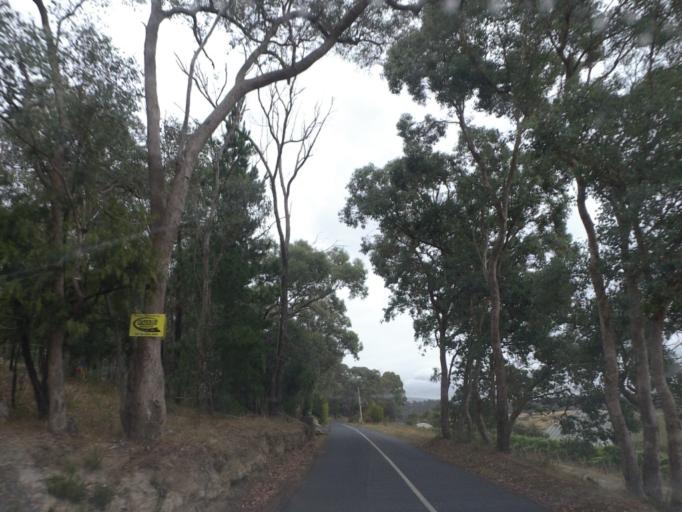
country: AU
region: Victoria
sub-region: Nillumbik
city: Saint Andrews
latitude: -37.6088
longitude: 145.3188
